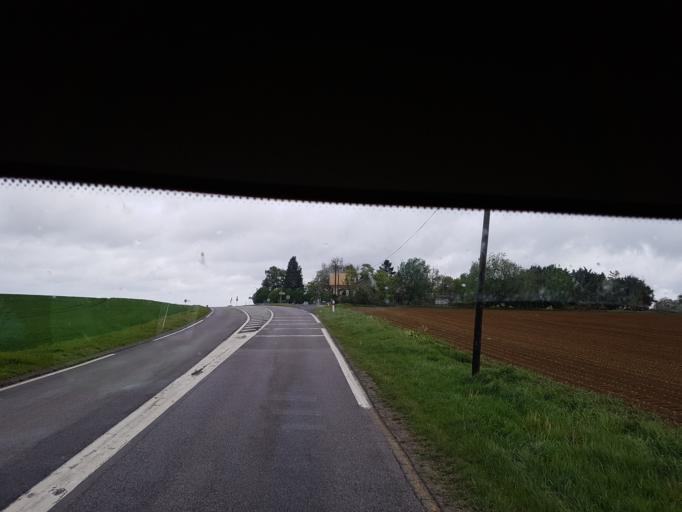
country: FR
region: Picardie
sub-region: Departement de l'Aisne
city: Crouy
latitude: 49.4444
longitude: 3.3584
